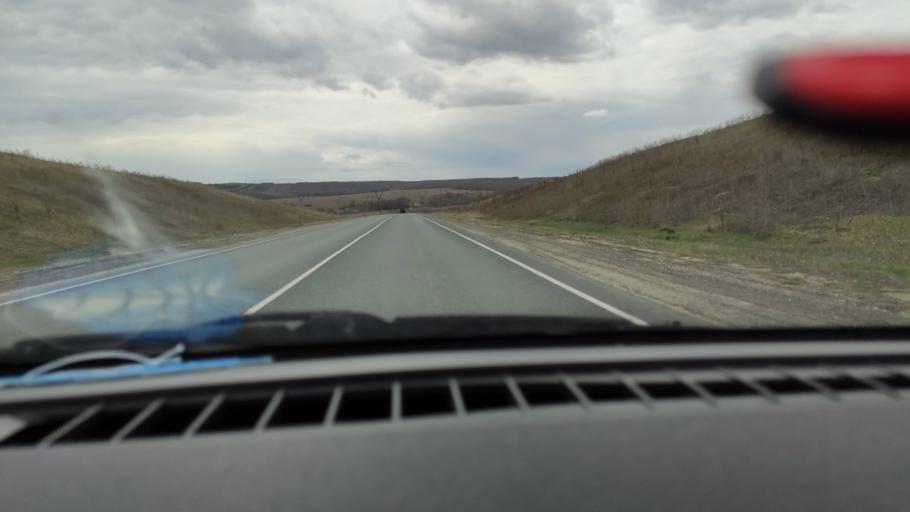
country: RU
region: Saratov
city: Sinodskoye
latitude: 51.9236
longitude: 46.5633
